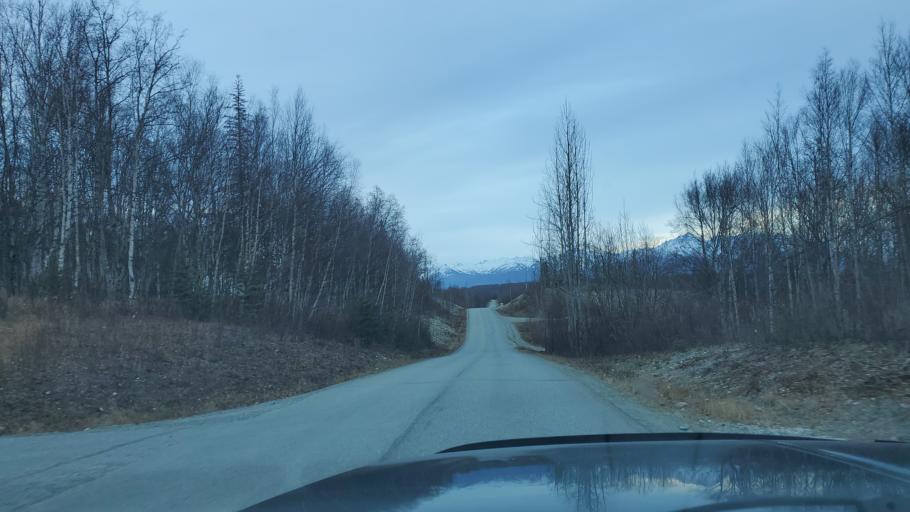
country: US
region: Alaska
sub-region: Matanuska-Susitna Borough
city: Lakes
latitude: 61.6572
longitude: -149.2944
